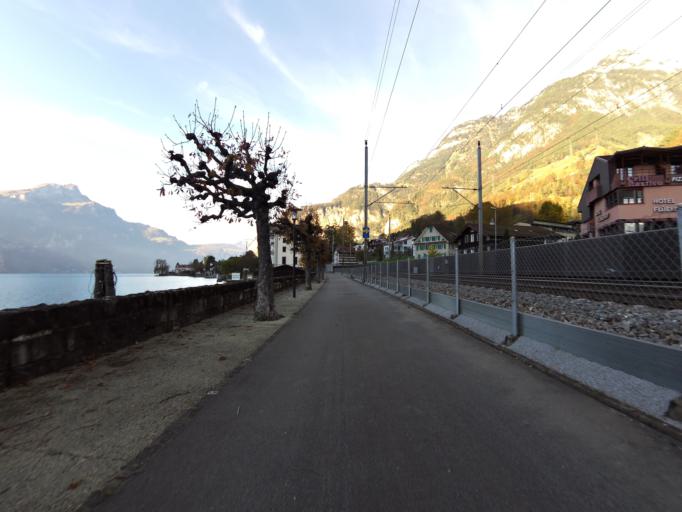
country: CH
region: Uri
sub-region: Uri
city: Flueelen
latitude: 46.9067
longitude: 8.6249
